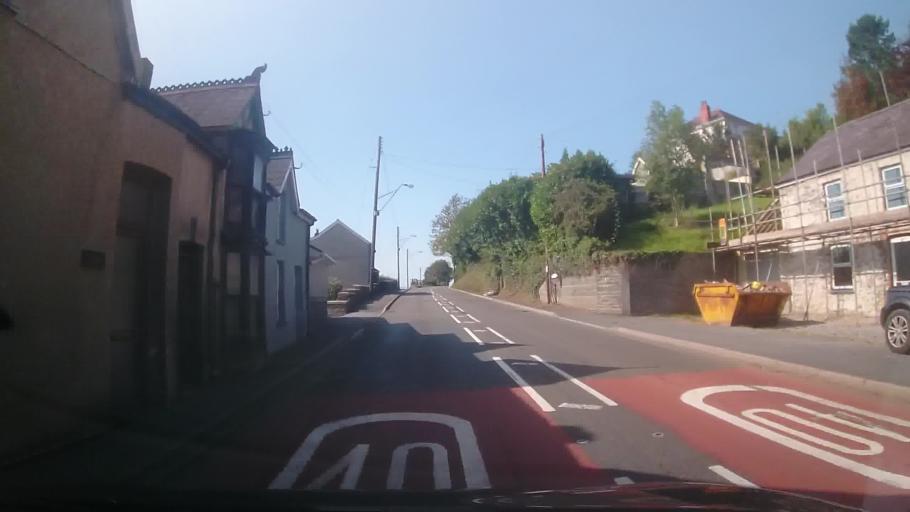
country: GB
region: Wales
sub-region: Carmarthenshire
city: Llanddarog
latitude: 51.8743
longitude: -4.1897
